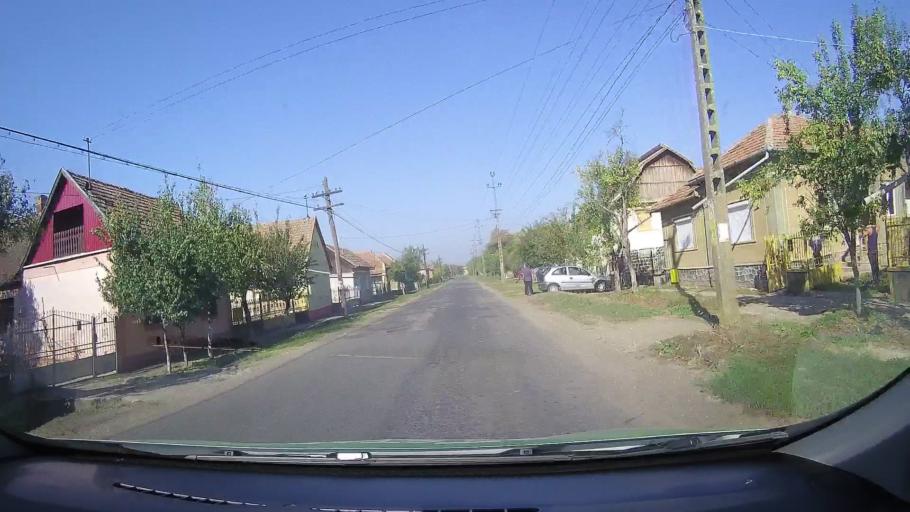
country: RO
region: Satu Mare
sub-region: Comuna Petresti
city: Petresti
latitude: 47.6069
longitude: 22.3600
